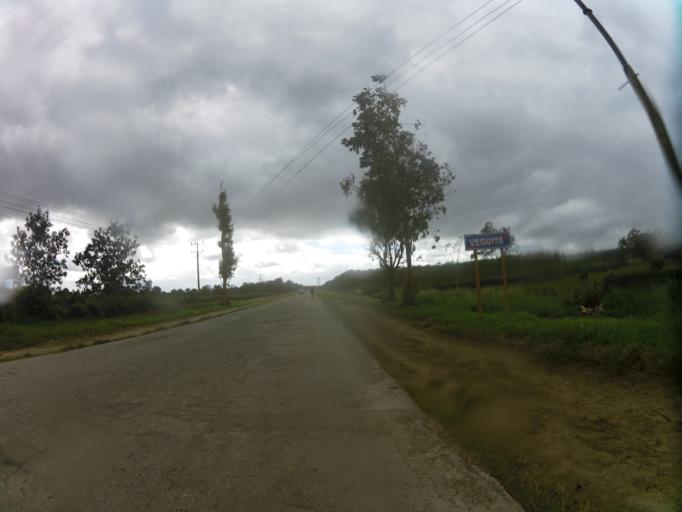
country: CU
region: Las Tunas
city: Las Tunas
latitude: 21.0411
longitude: -76.9329
